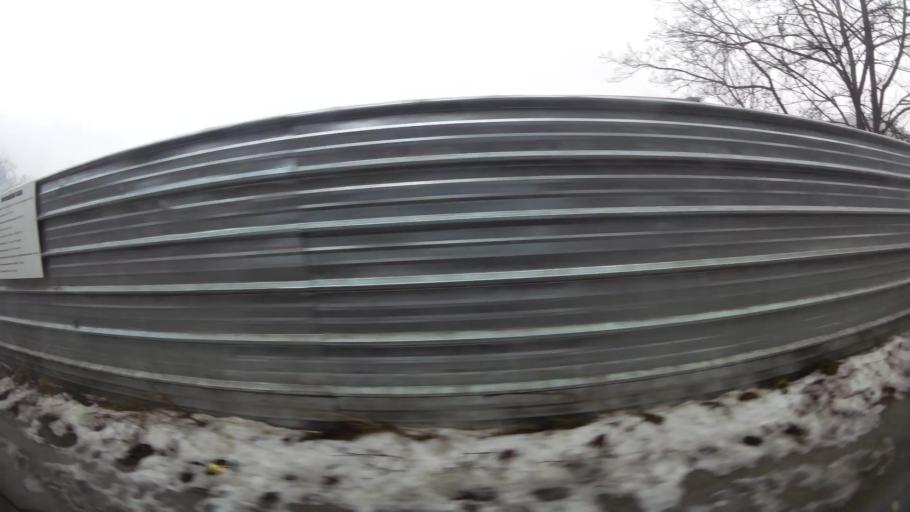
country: BG
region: Sofia-Capital
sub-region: Stolichna Obshtina
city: Sofia
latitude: 42.6530
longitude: 23.2538
